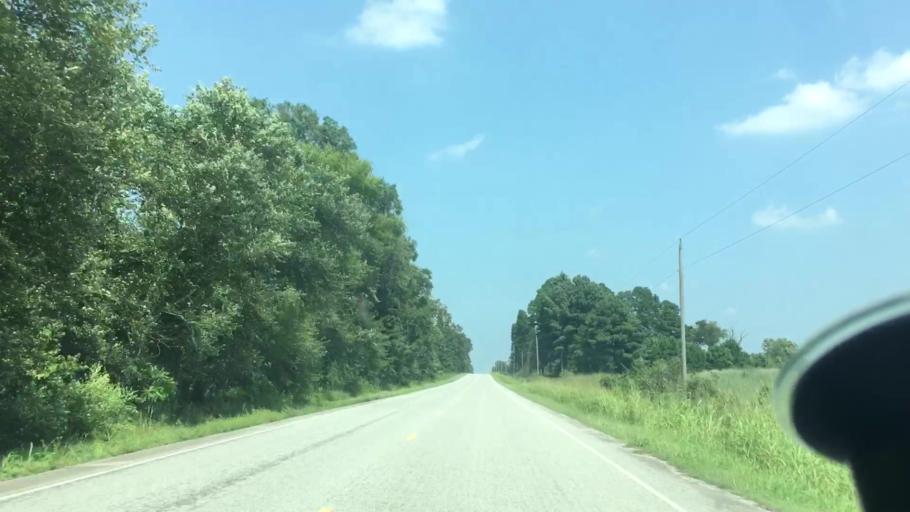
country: US
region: Oklahoma
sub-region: Atoka County
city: Atoka
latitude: 34.2602
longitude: -95.9361
